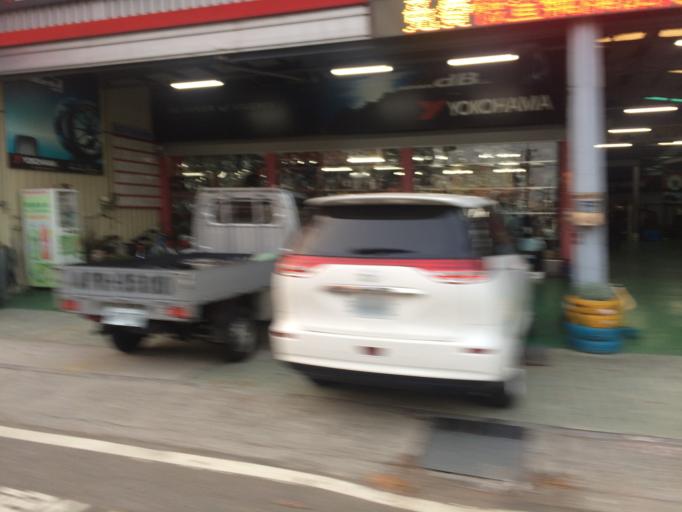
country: TW
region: Taiwan
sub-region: Hsinchu
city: Hsinchu
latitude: 24.6969
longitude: 120.9174
